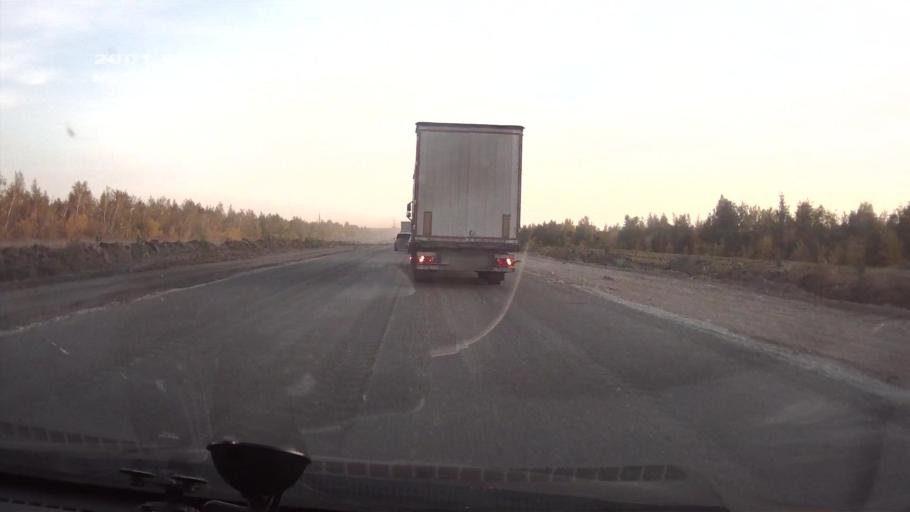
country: RU
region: Saratov
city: Kamenskiy
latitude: 50.9289
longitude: 45.5996
